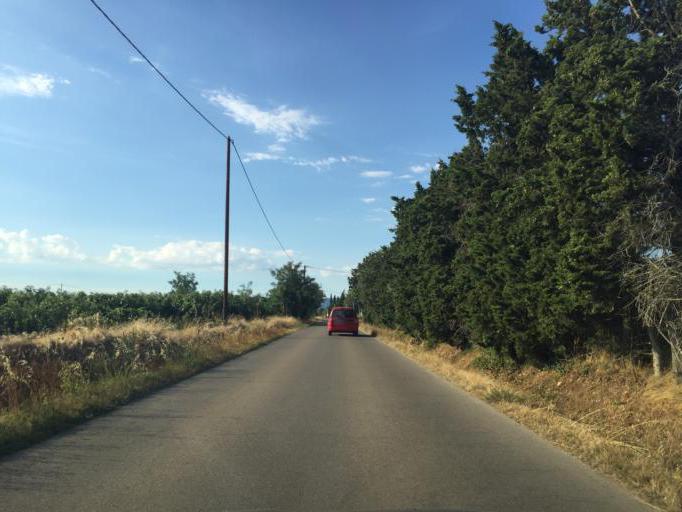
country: FR
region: Provence-Alpes-Cote d'Azur
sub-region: Departement du Vaucluse
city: Pernes-les-Fontaines
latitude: 44.0176
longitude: 5.0548
